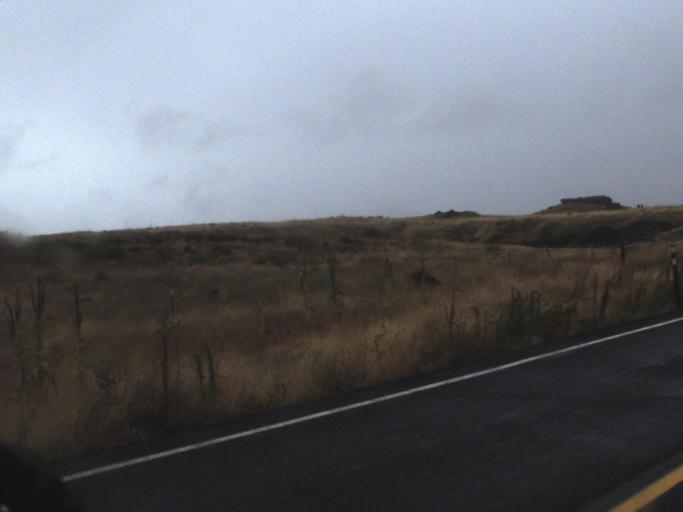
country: US
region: Washington
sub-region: Spokane County
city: Medical Lake
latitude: 47.2521
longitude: -117.9290
